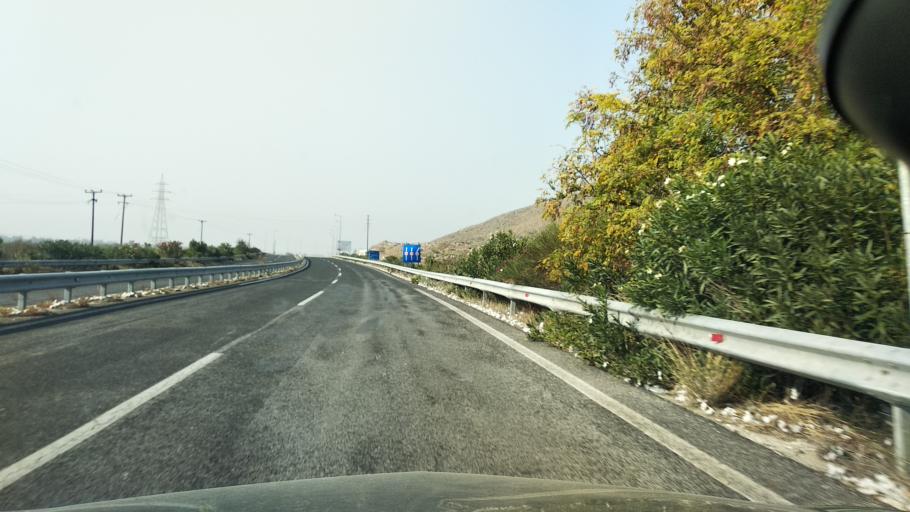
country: GR
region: Thessaly
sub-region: Trikala
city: Farkadona
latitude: 39.5900
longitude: 22.0858
